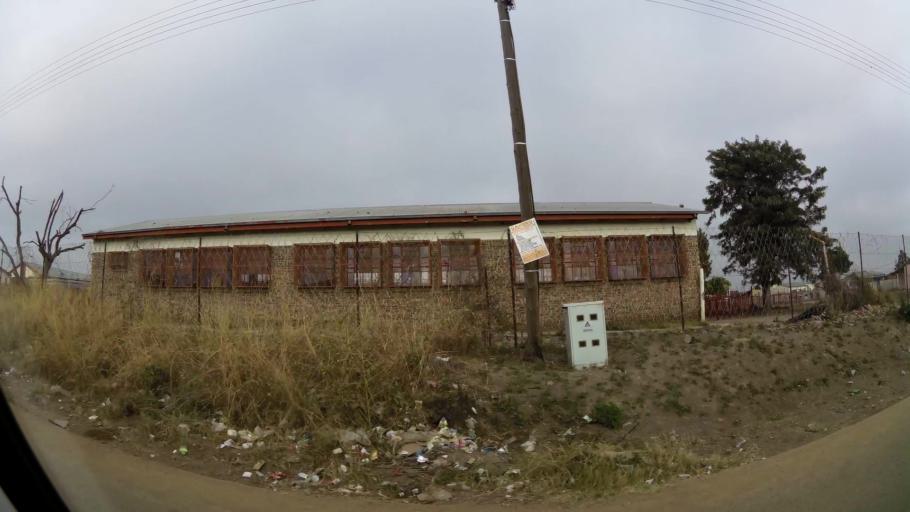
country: ZA
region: Limpopo
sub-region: Capricorn District Municipality
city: Polokwane
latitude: -23.8409
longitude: 29.3852
